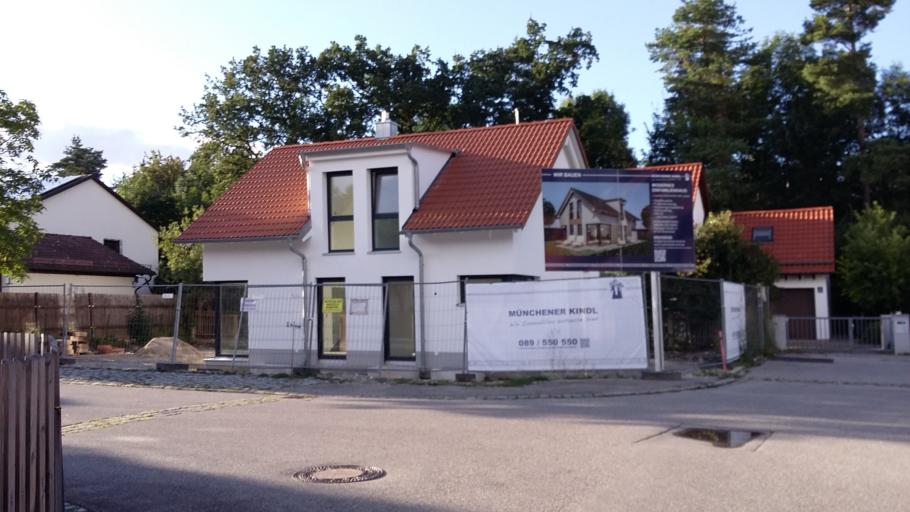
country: DE
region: Bavaria
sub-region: Upper Bavaria
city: Neuried
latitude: 48.0967
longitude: 11.4710
